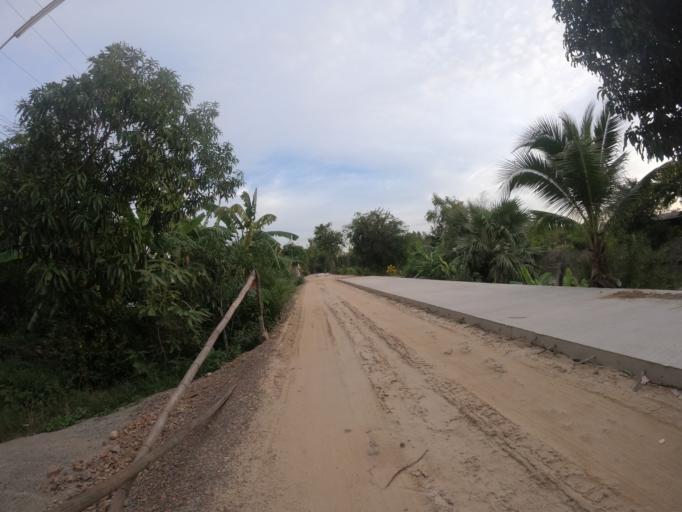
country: TH
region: Pathum Thani
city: Ban Rangsit
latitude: 14.0204
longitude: 100.7999
